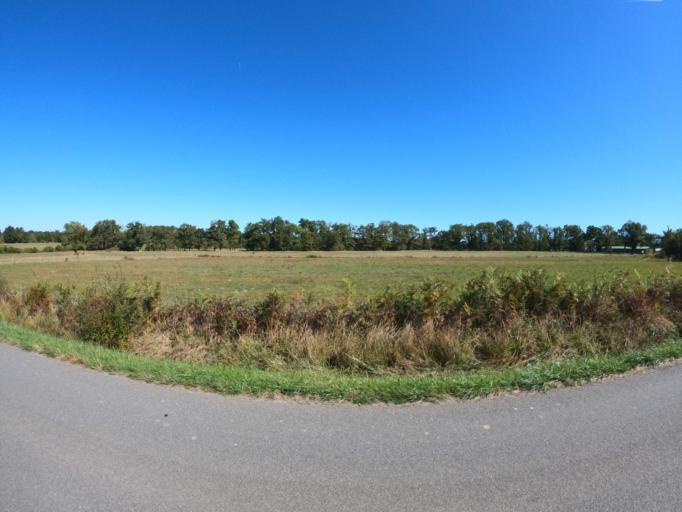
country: FR
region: Limousin
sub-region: Departement de la Haute-Vienne
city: Le Dorat
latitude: 46.2710
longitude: 1.0241
